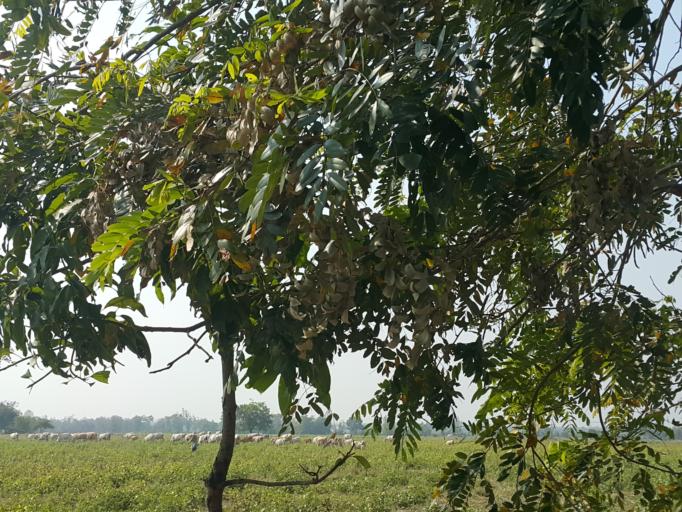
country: TH
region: Chiang Mai
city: San Kamphaeng
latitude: 18.7792
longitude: 99.1408
